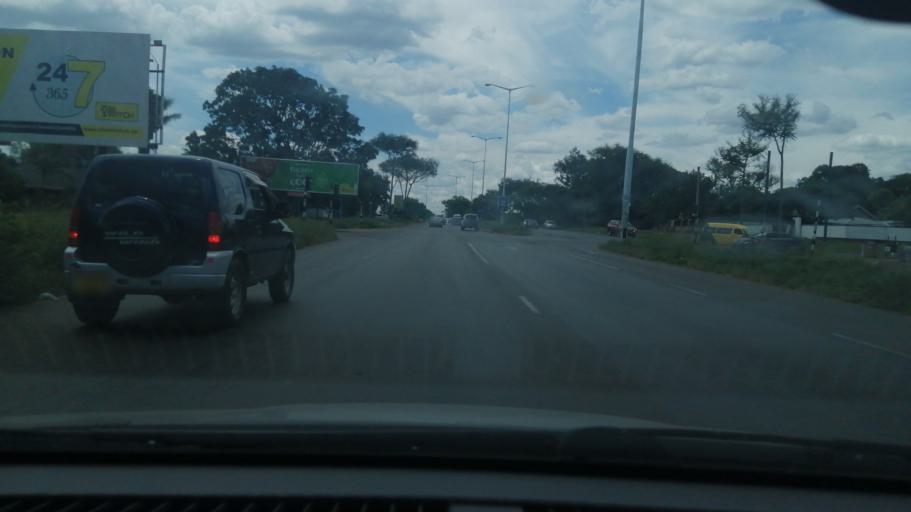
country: ZW
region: Harare
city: Harare
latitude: -17.8261
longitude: 31.0965
